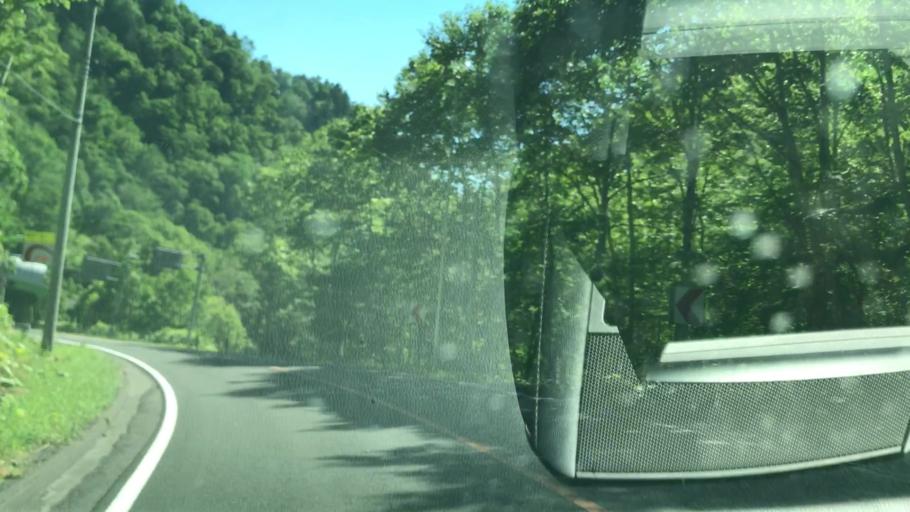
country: JP
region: Hokkaido
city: Shimo-furano
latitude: 42.9651
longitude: 142.6235
